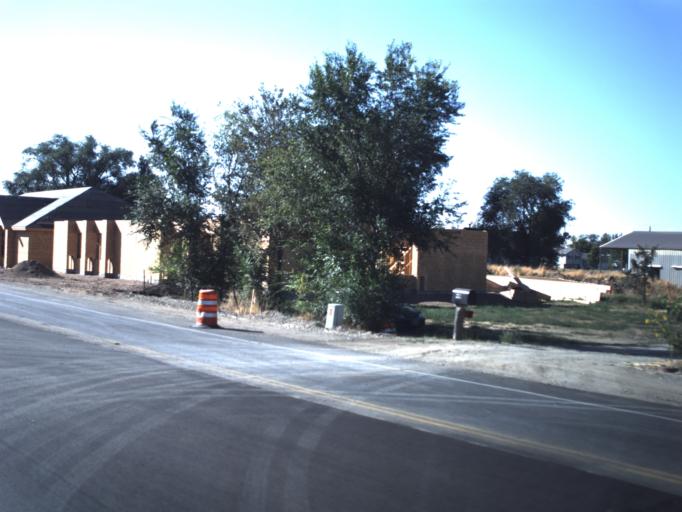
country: US
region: Utah
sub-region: Weber County
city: Hooper
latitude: 41.1908
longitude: -112.1013
